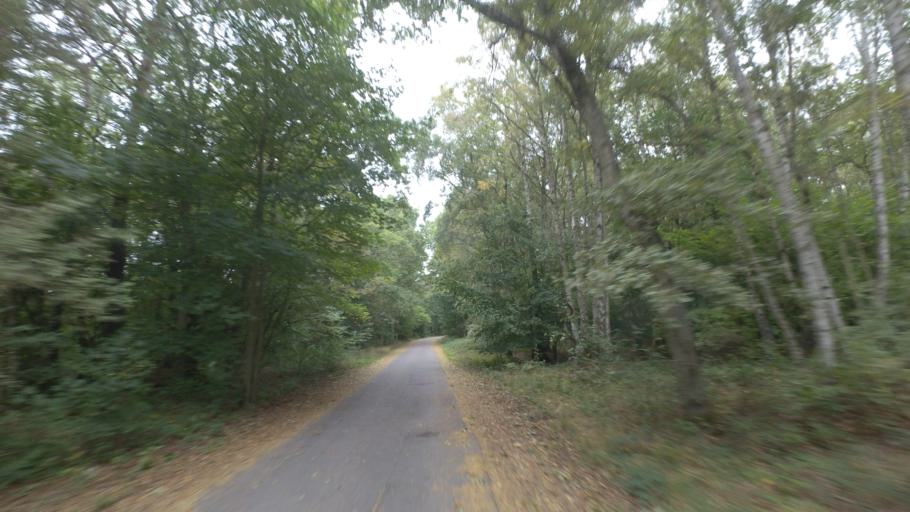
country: DK
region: Capital Region
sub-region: Bornholm Kommune
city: Nexo
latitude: 55.0009
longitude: 15.0384
